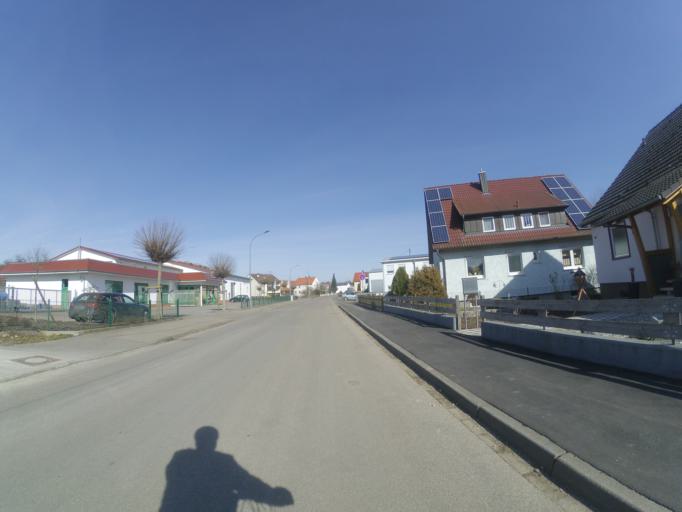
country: DE
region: Baden-Wuerttemberg
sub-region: Regierungsbezirk Stuttgart
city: Niederstotzingen
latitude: 48.5336
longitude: 10.2328
